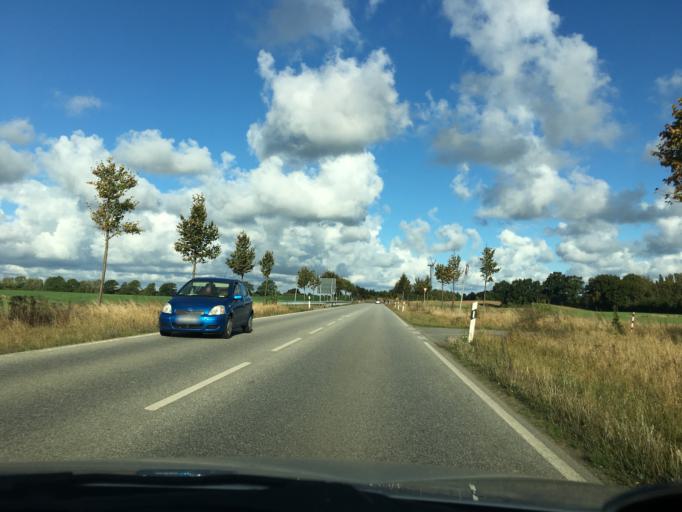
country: DE
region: Schleswig-Holstein
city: Brodersdorf
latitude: 54.3864
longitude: 10.2437
